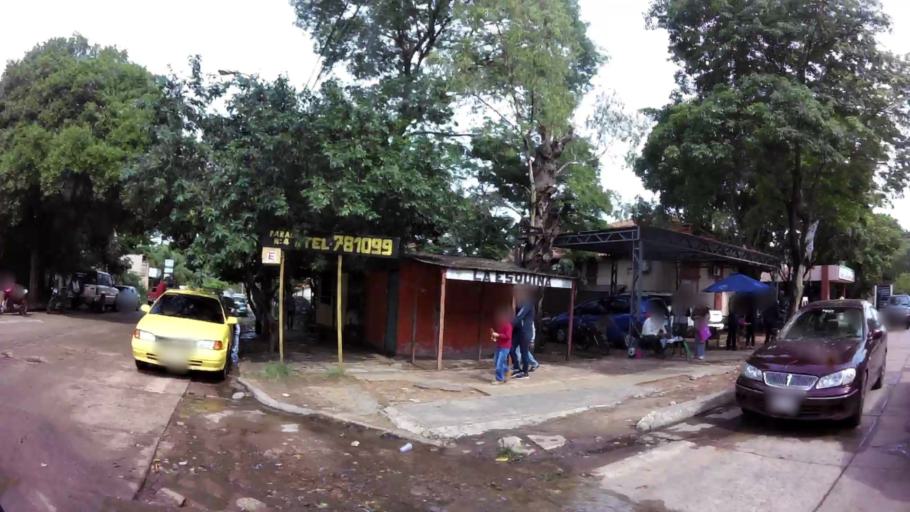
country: PY
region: Central
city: Limpio
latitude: -25.1648
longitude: -57.4759
